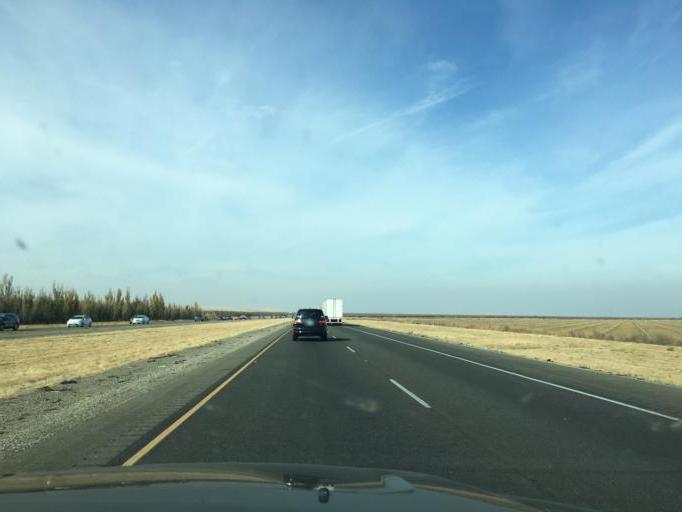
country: US
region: California
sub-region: Merced County
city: South Dos Palos
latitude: 36.7995
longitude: -120.7388
